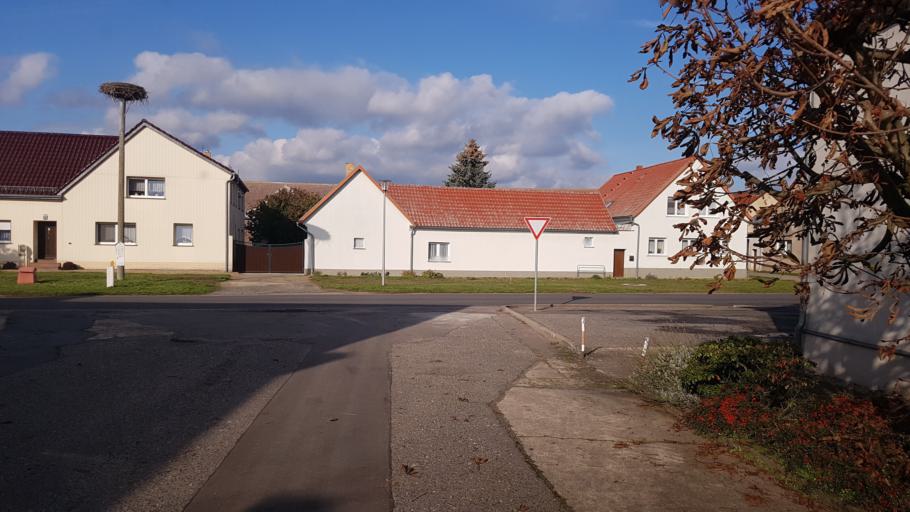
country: DE
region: Brandenburg
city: Schonewalde
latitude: 51.6908
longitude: 13.5363
